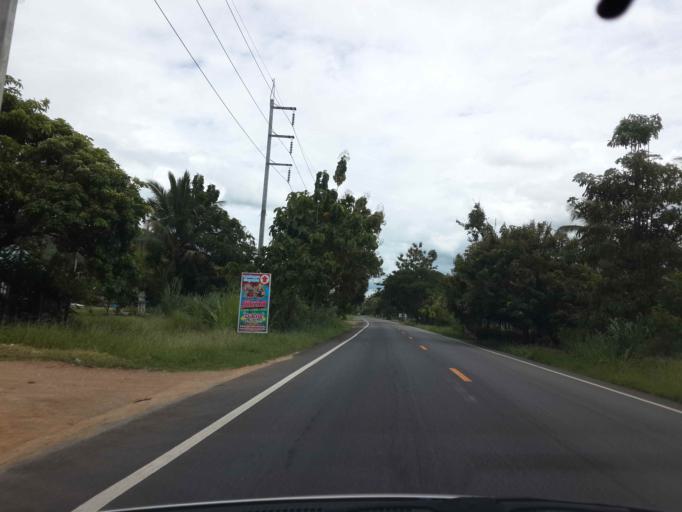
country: TH
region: Ratchaburi
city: Suan Phueng
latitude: 13.5484
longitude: 99.4728
